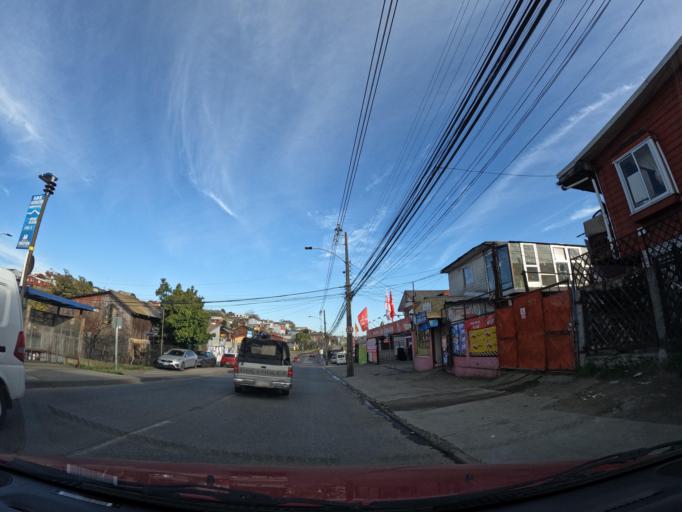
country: CL
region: Biobio
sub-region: Provincia de Concepcion
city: Concepcion
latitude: -36.7927
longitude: -73.0457
